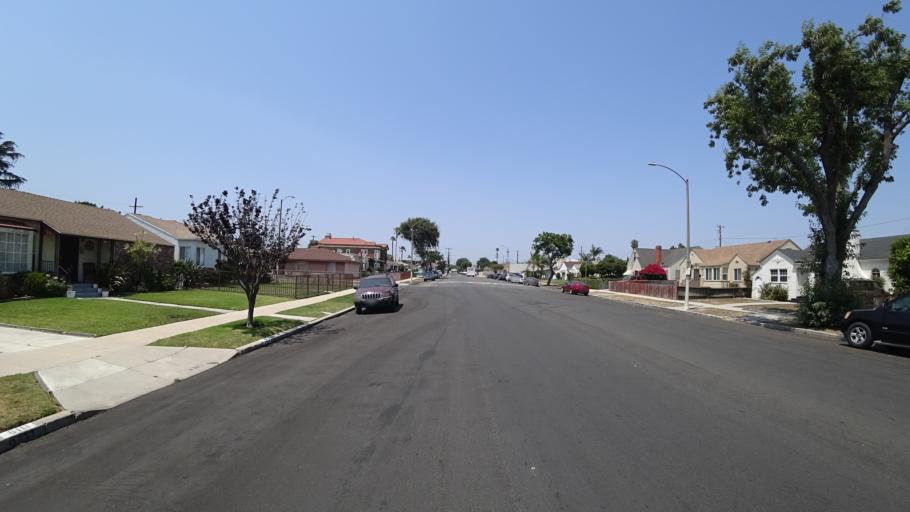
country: US
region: California
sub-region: Los Angeles County
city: View Park-Windsor Hills
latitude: 33.9841
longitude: -118.3440
